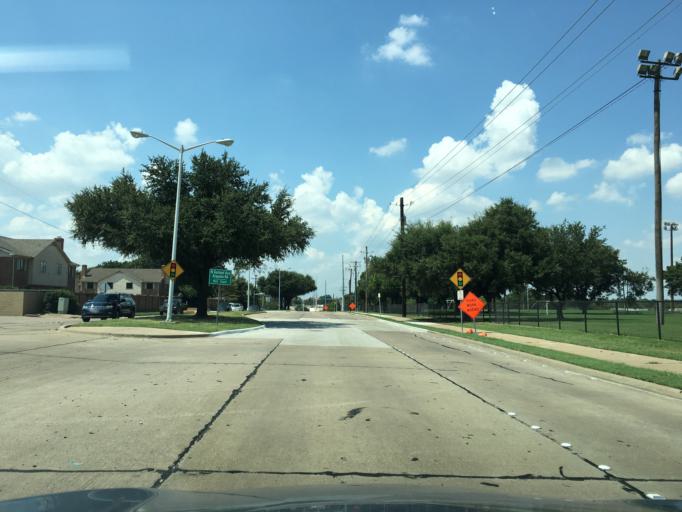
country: US
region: Texas
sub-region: Dallas County
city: Garland
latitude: 32.9526
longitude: -96.6547
